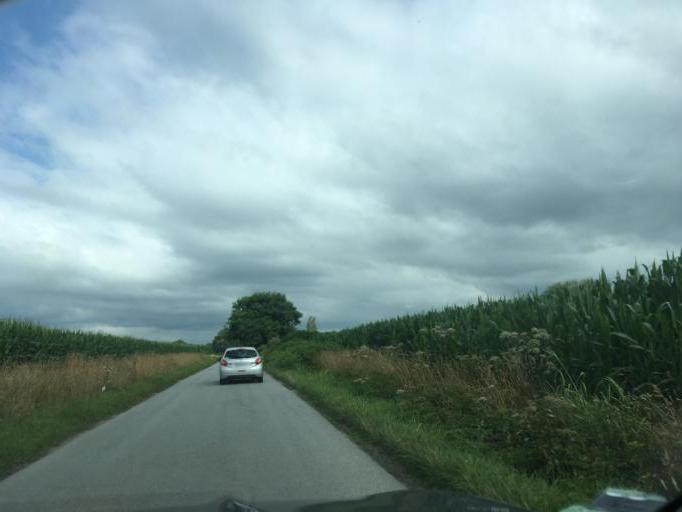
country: FR
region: Aquitaine
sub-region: Departement des Pyrenees-Atlantiques
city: Buros
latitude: 43.3145
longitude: -0.2898
